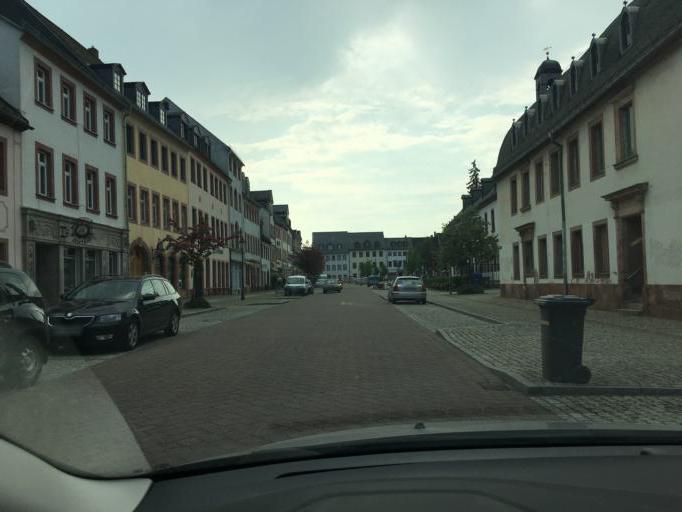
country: DE
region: Saxony
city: Rochlitz
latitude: 51.0456
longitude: 12.8010
